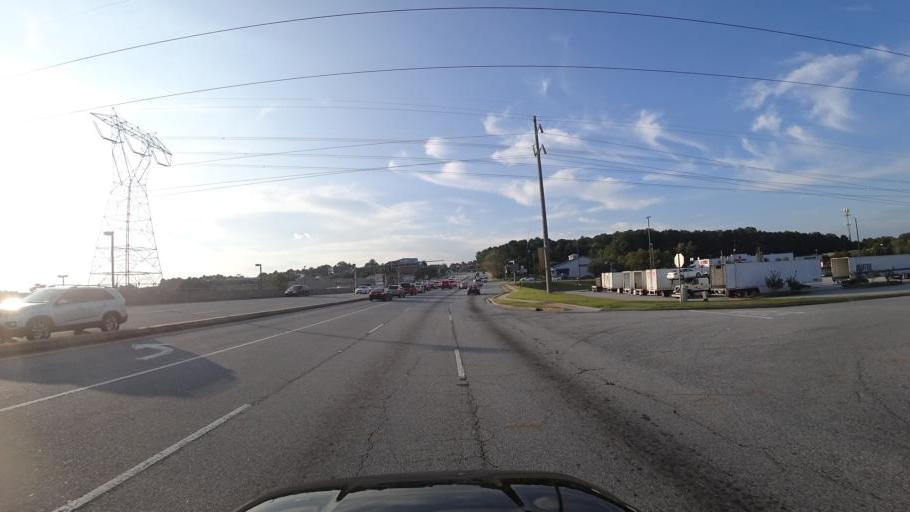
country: US
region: Georgia
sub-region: Gwinnett County
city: Duluth
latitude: 33.9502
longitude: -84.1387
